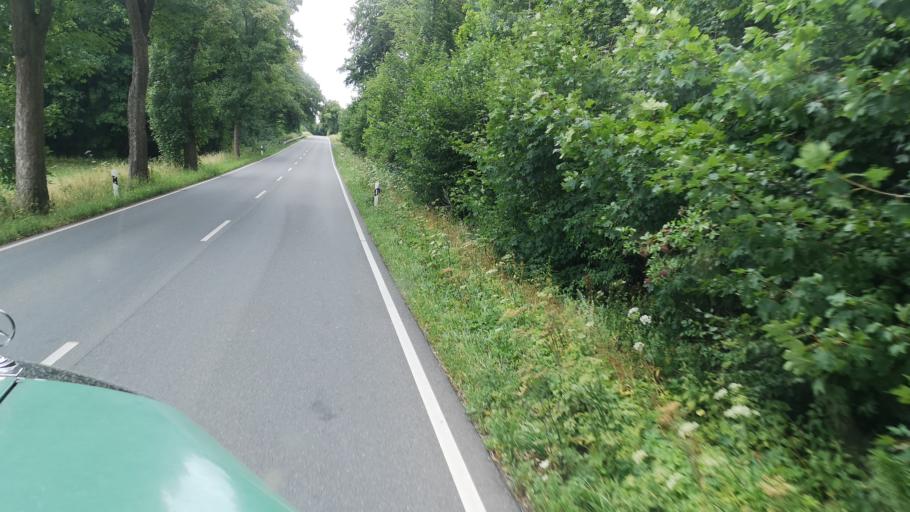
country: DE
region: North Rhine-Westphalia
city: Huckeswagen
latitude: 51.1552
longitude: 7.2834
